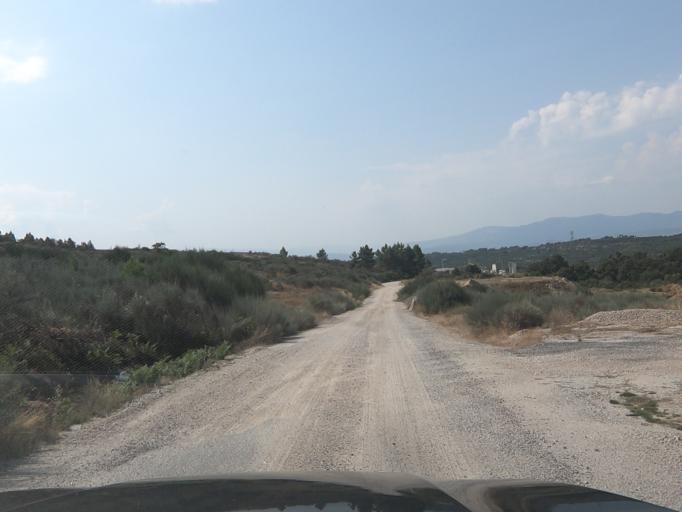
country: PT
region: Vila Real
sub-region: Sabrosa
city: Sabrosa
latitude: 41.3117
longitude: -7.6242
